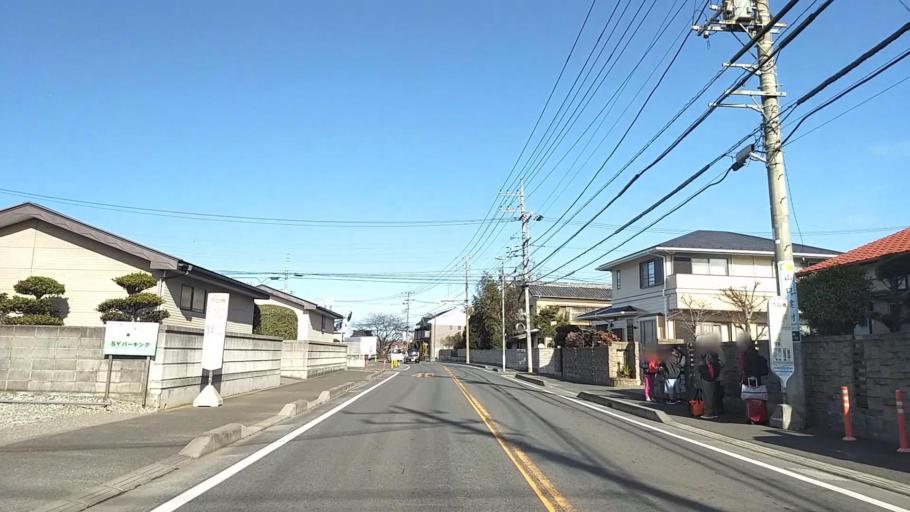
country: JP
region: Kanagawa
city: Atsugi
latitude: 35.4600
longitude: 139.3475
